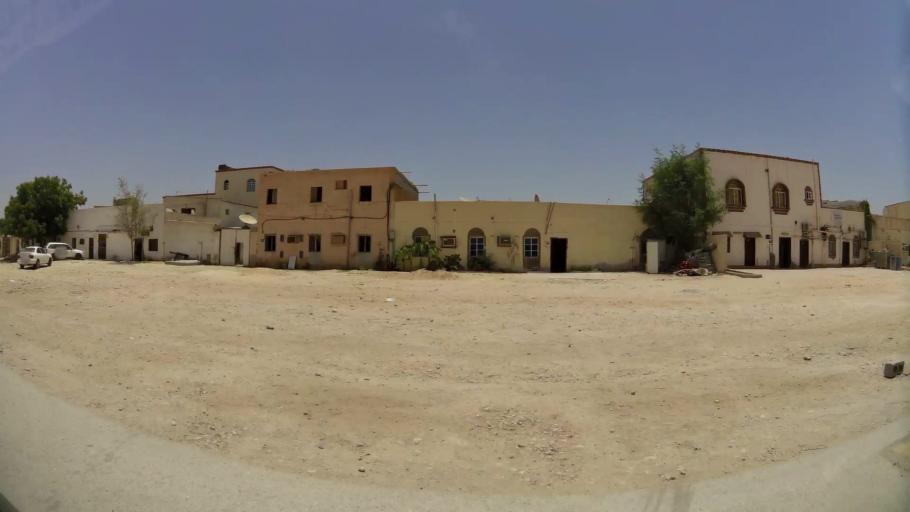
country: OM
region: Zufar
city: Salalah
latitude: 17.0790
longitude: 54.1534
